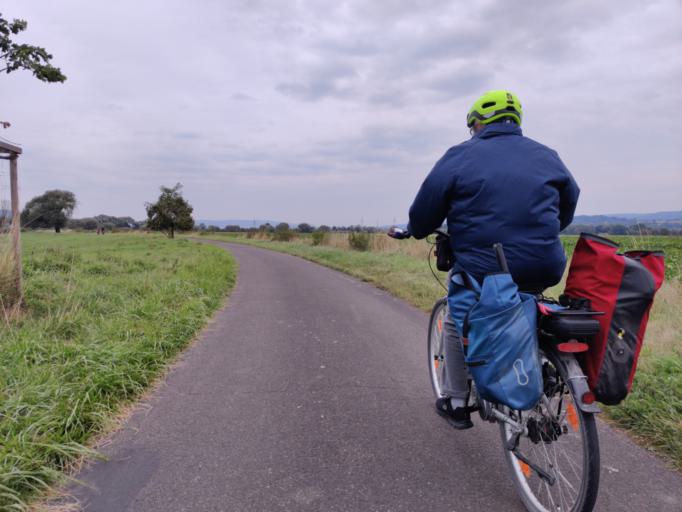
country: DE
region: Lower Saxony
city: Holzminden
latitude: 51.8028
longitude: 9.4125
